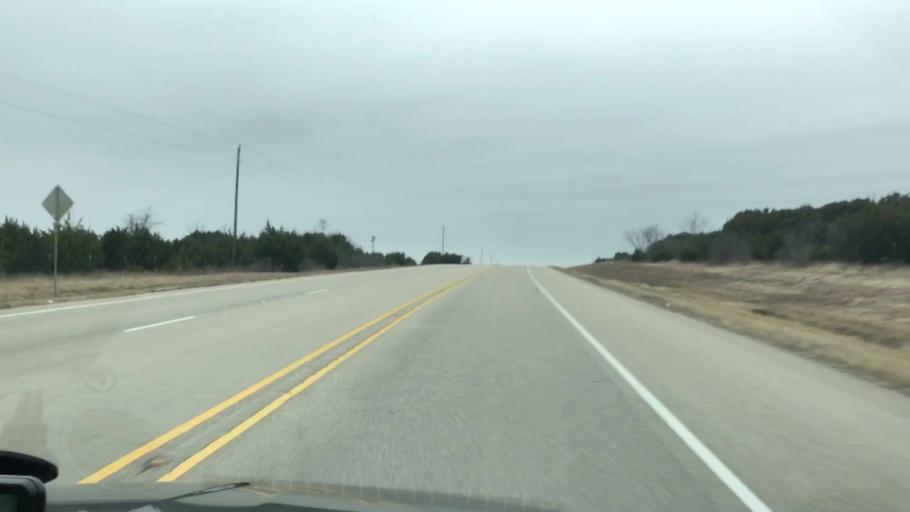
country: US
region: Texas
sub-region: Hamilton County
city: Hamilton
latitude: 31.8421
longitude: -98.1147
